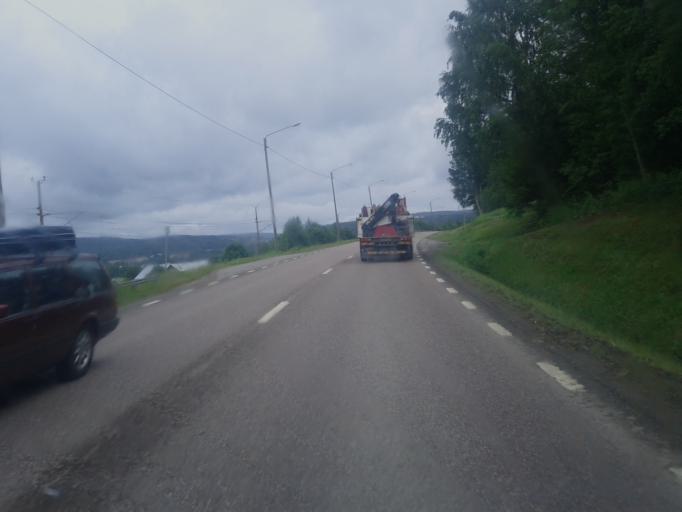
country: SE
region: Vaesternorrland
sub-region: Sundsvalls Kommun
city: Vi
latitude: 62.3962
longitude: 17.1989
